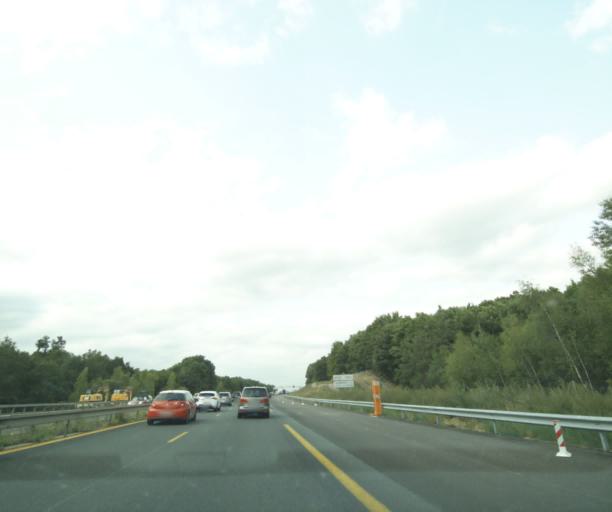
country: FR
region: Centre
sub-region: Departement d'Indre-et-Loire
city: Chambray-les-Tours
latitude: 47.3166
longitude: 0.6891
